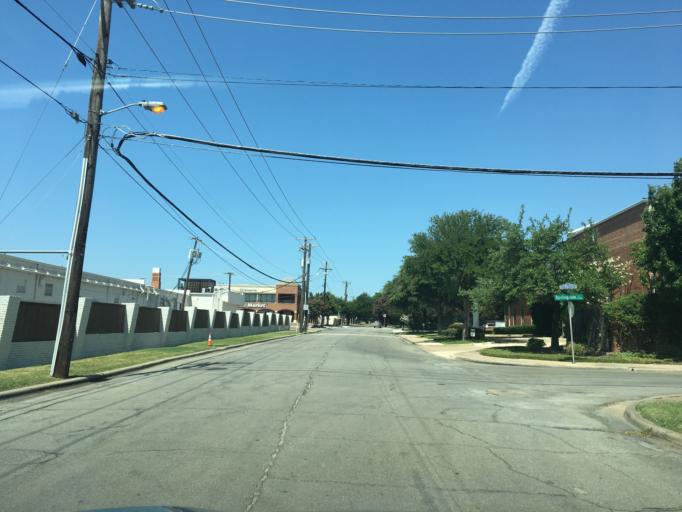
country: US
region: Texas
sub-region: Dallas County
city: Highland Park
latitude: 32.8383
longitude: -96.7511
